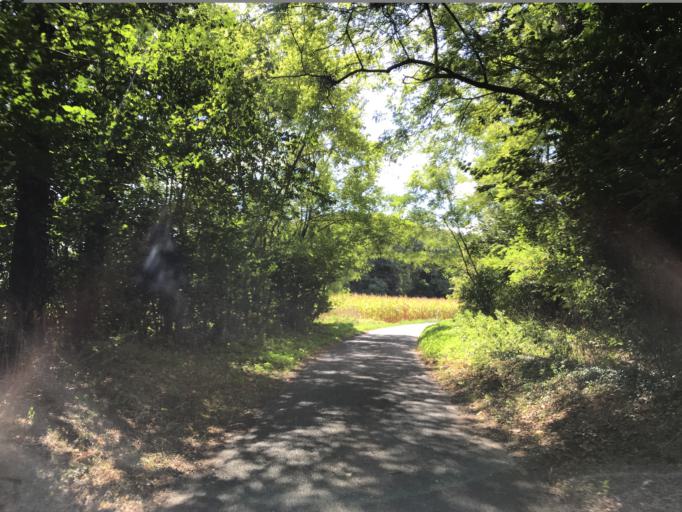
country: FR
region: Haute-Normandie
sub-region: Departement de l'Eure
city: Saint-Just
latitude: 49.1496
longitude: 1.4061
